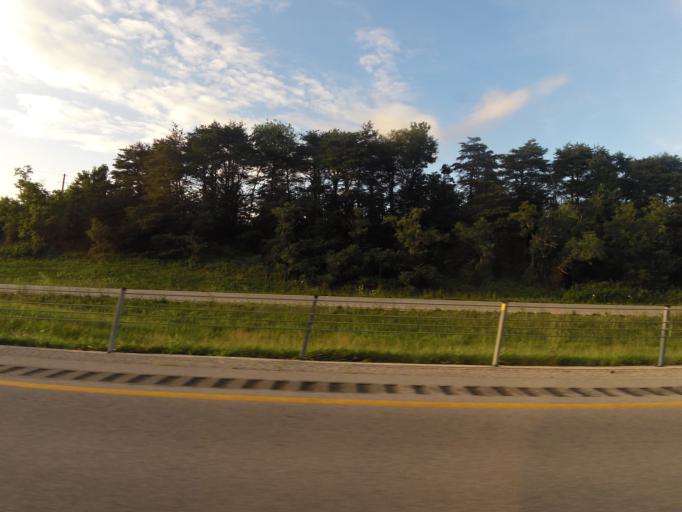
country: US
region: Kentucky
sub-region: Laurel County
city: London
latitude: 37.2049
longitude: -84.1636
